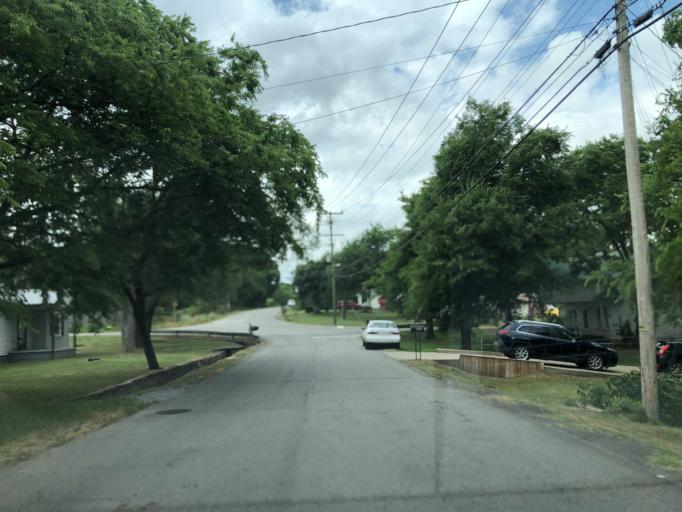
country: US
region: Tennessee
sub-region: Davidson County
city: Lakewood
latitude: 36.2660
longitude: -86.6912
